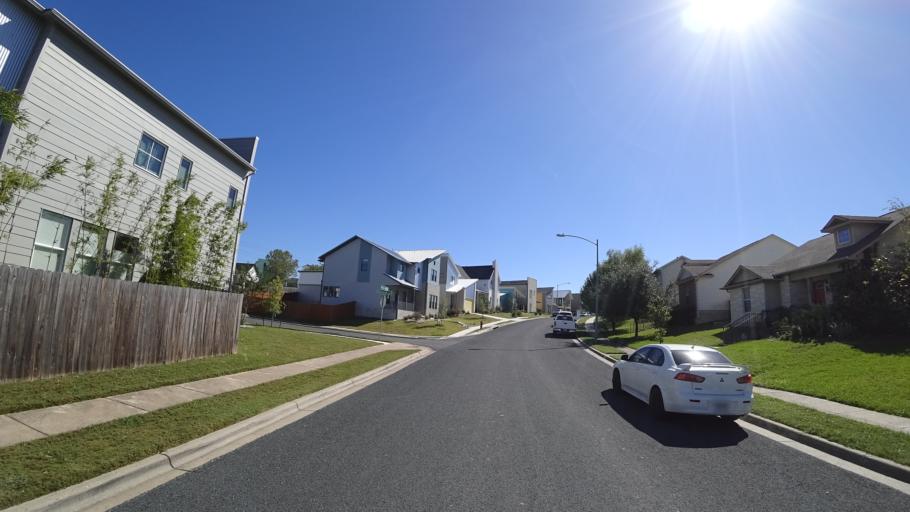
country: US
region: Texas
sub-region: Travis County
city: Hornsby Bend
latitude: 30.2904
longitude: -97.6438
